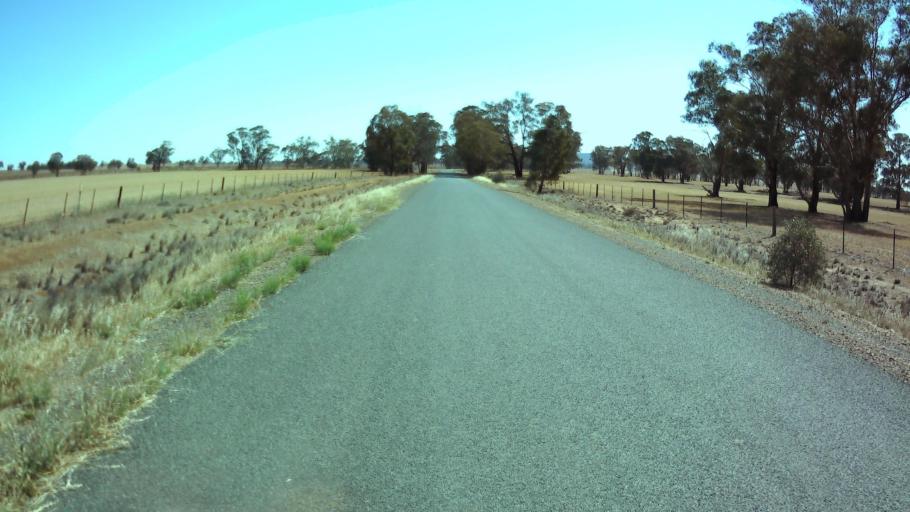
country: AU
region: New South Wales
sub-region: Weddin
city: Grenfell
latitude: -33.7323
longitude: 147.8876
